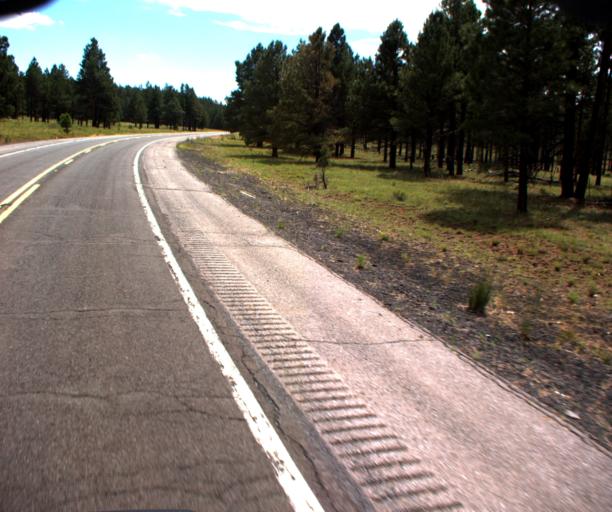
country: US
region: Arizona
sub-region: Coconino County
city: Parks
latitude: 35.4427
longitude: -111.7615
